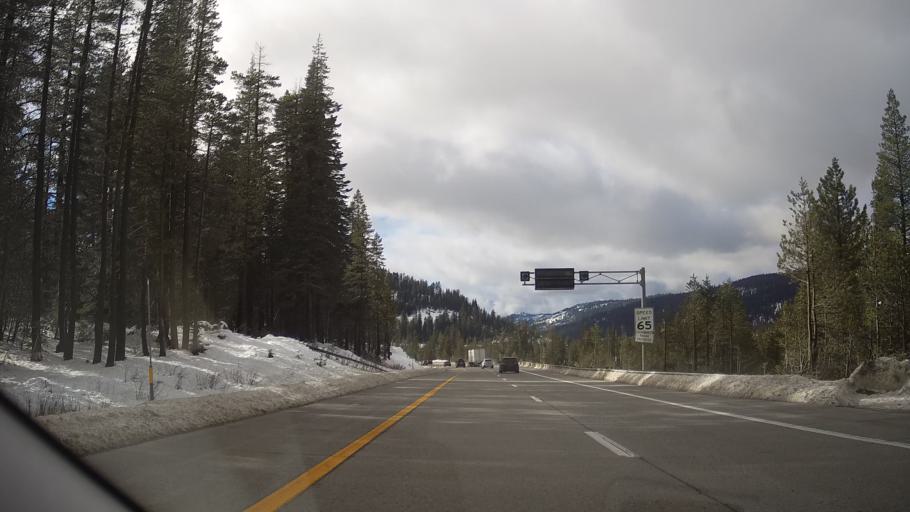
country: US
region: California
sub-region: Nevada County
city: Truckee
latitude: 39.3241
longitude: -120.3977
